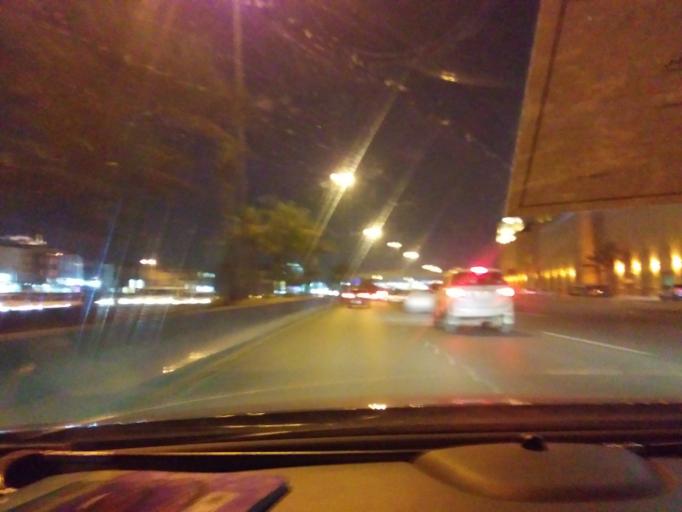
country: SA
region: Ar Riyad
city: Riyadh
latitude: 24.6758
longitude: 46.7786
